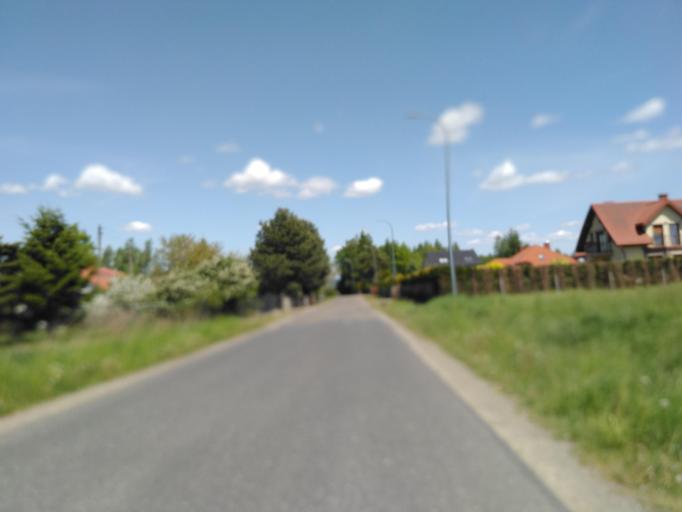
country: PL
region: Subcarpathian Voivodeship
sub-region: Powiat krosnienski
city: Jedlicze
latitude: 49.7046
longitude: 21.6894
